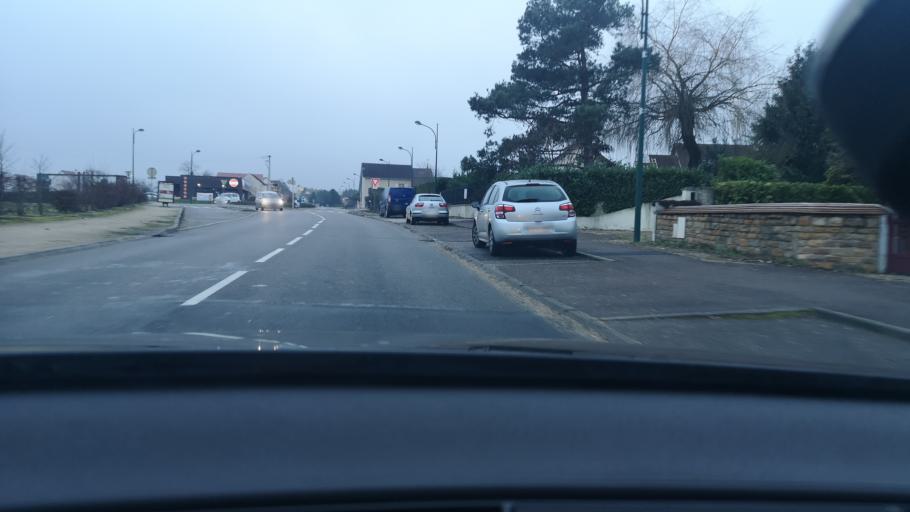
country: FR
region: Bourgogne
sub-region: Departement de la Cote-d'Or
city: Fenay
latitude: 47.1963
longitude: 5.0825
